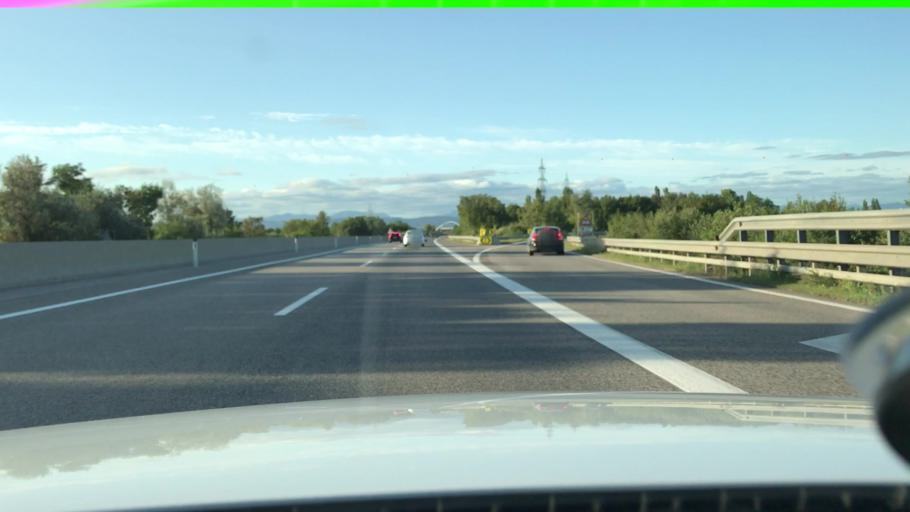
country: AT
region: Lower Austria
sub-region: Politischer Bezirk Sankt Polten
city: Herzogenburg
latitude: 48.2326
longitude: 15.6817
